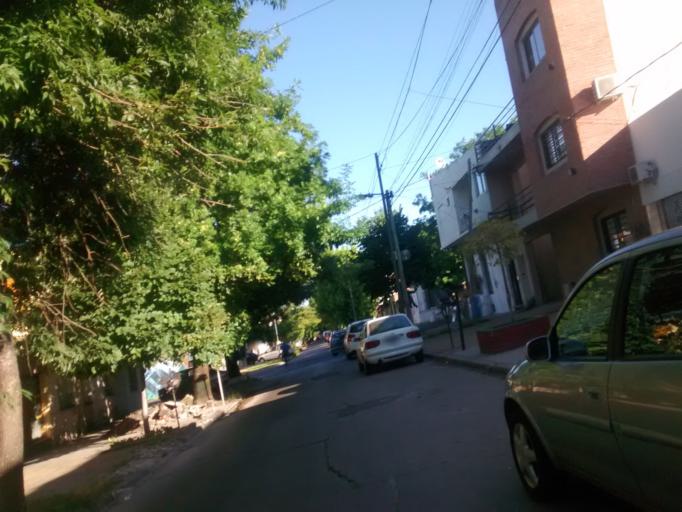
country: AR
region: Buenos Aires
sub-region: Partido de La Plata
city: La Plata
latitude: -34.9324
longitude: -57.9467
